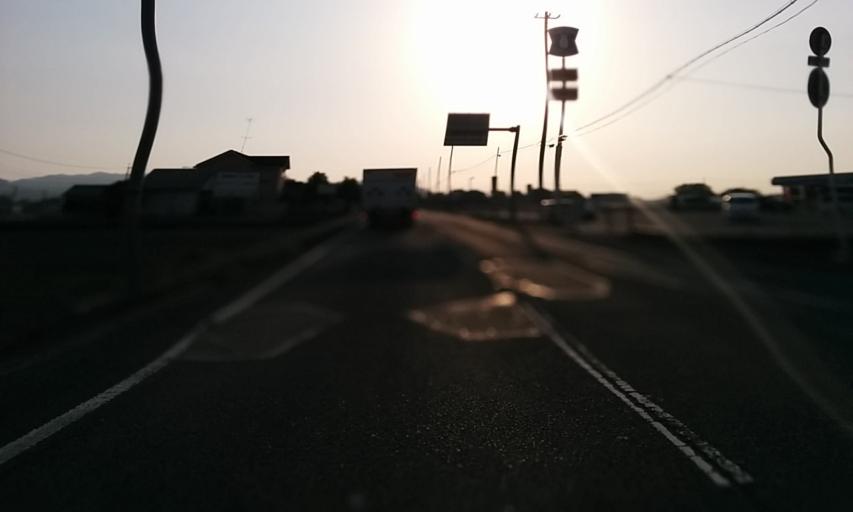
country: JP
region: Ehime
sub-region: Shikoku-chuo Shi
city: Matsuyama
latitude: 33.7785
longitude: 132.8321
